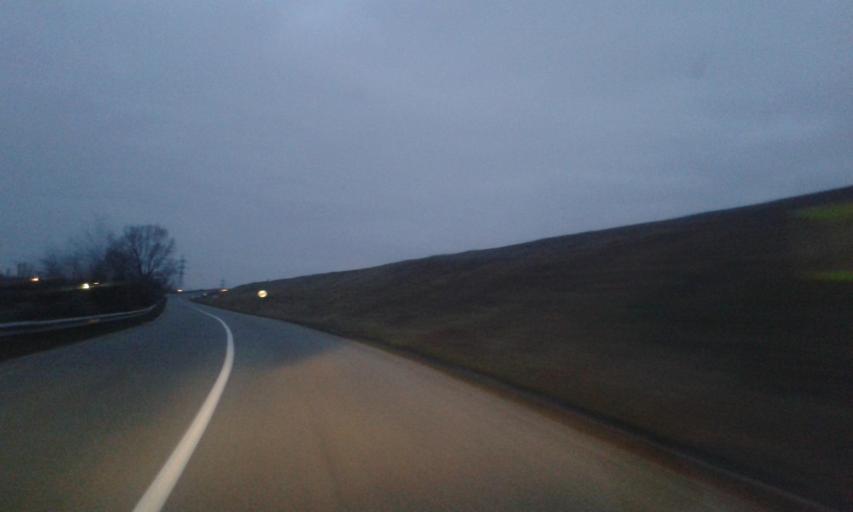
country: RO
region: Gorj
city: Targu Jiu
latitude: 45.0618
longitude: 23.2741
